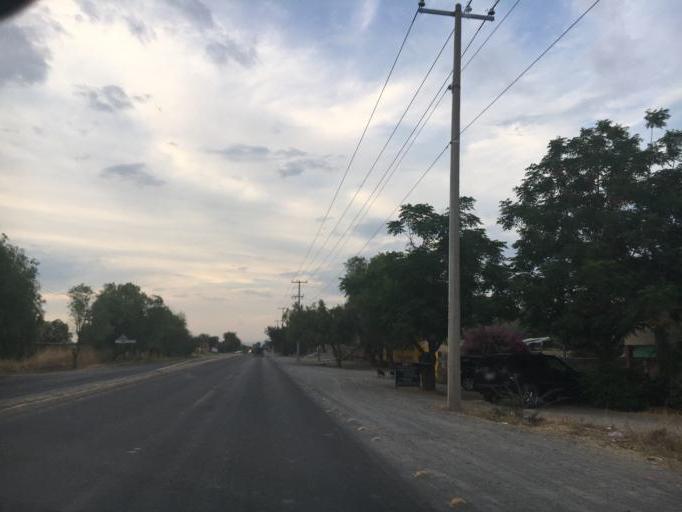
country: MX
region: Guanajuato
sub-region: Leon
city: El CERESO
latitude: 20.9861
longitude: -101.7021
